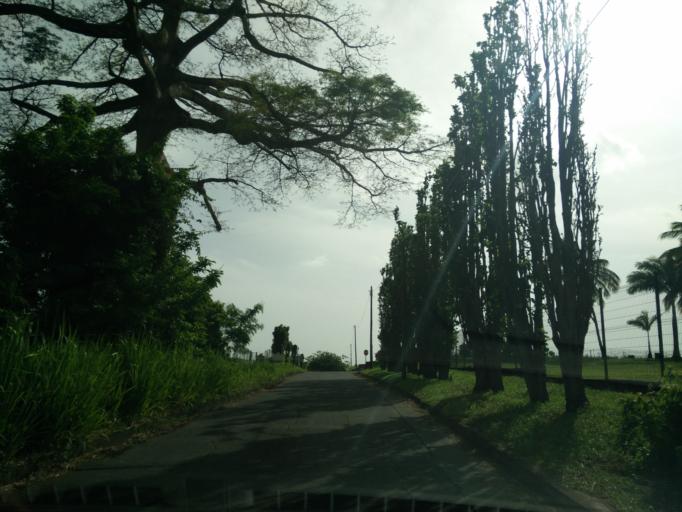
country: MQ
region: Martinique
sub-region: Martinique
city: Saint-Pierre
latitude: 14.7558
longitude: -61.1653
